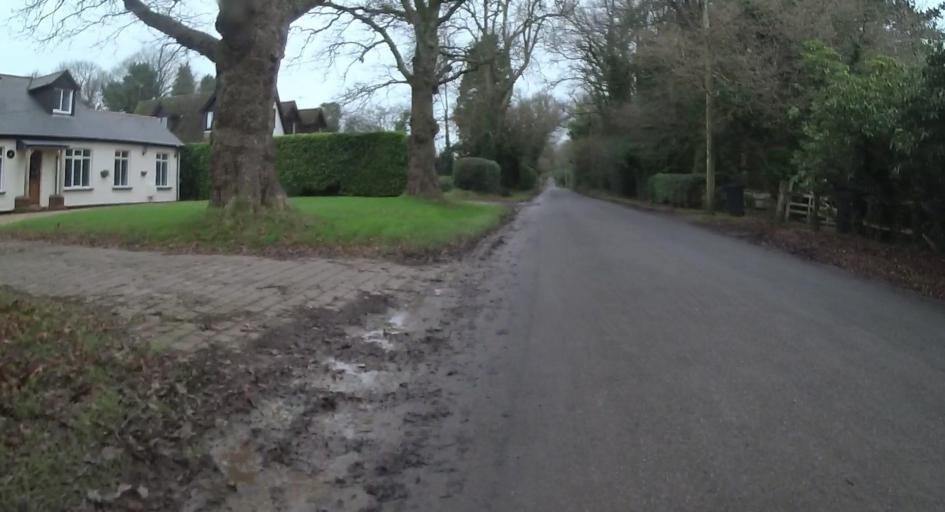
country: GB
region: England
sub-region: Hampshire
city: Four Marks
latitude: 51.1028
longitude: -1.0418
